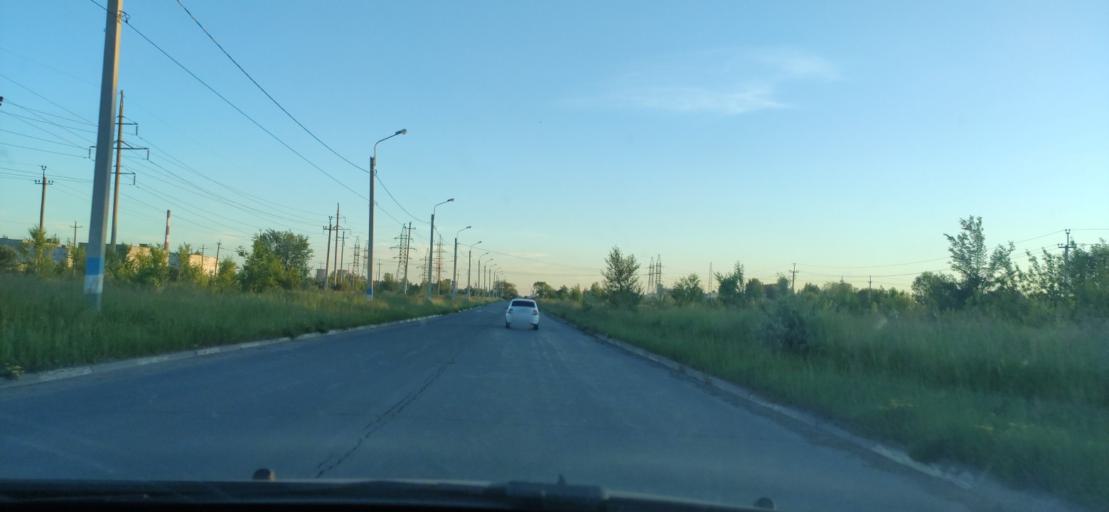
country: RU
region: Ulyanovsk
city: Mirnyy
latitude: 54.3712
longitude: 48.6454
